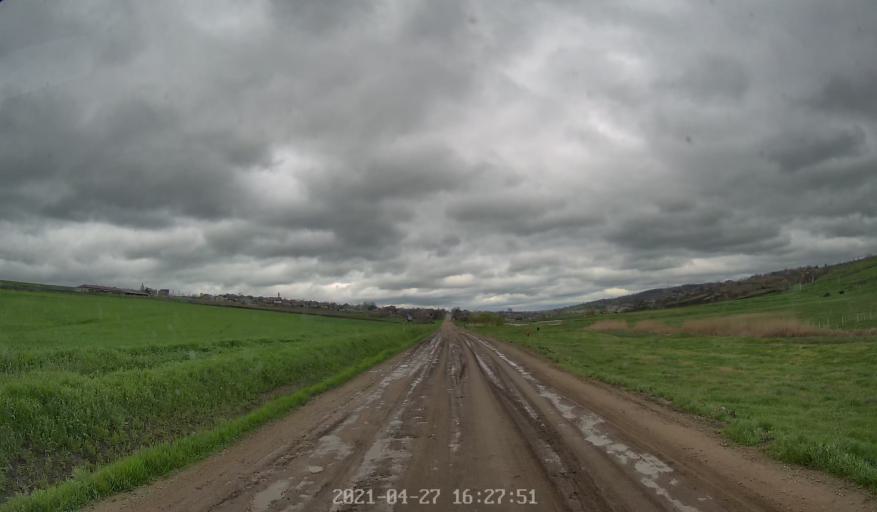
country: MD
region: Chisinau
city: Singera
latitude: 46.9740
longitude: 29.0372
